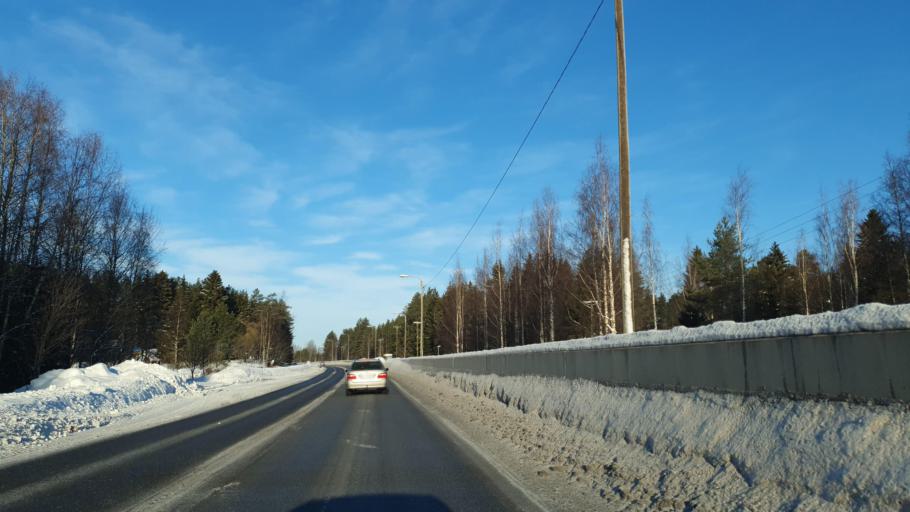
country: FI
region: Northern Ostrobothnia
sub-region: Oulu
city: Kempele
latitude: 64.9664
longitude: 25.6299
